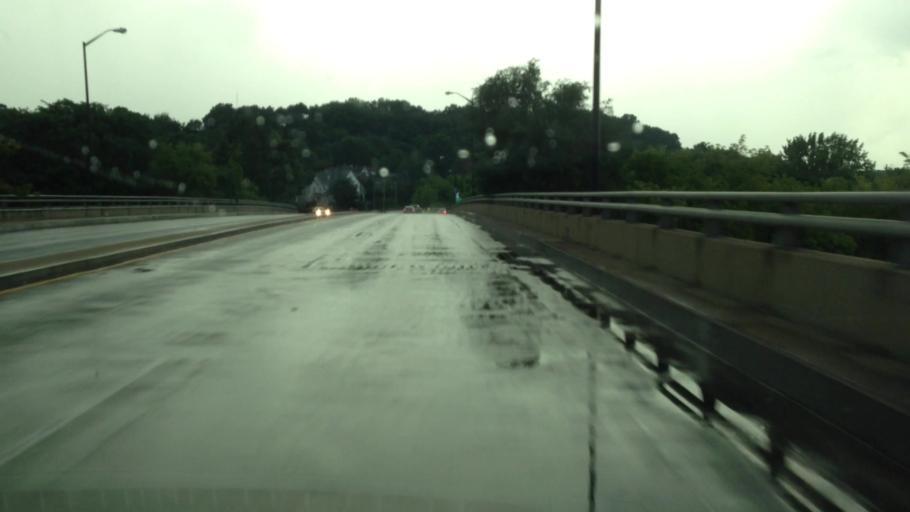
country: US
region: Ohio
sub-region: Summit County
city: Portage Lakes
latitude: 41.0423
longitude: -81.5464
